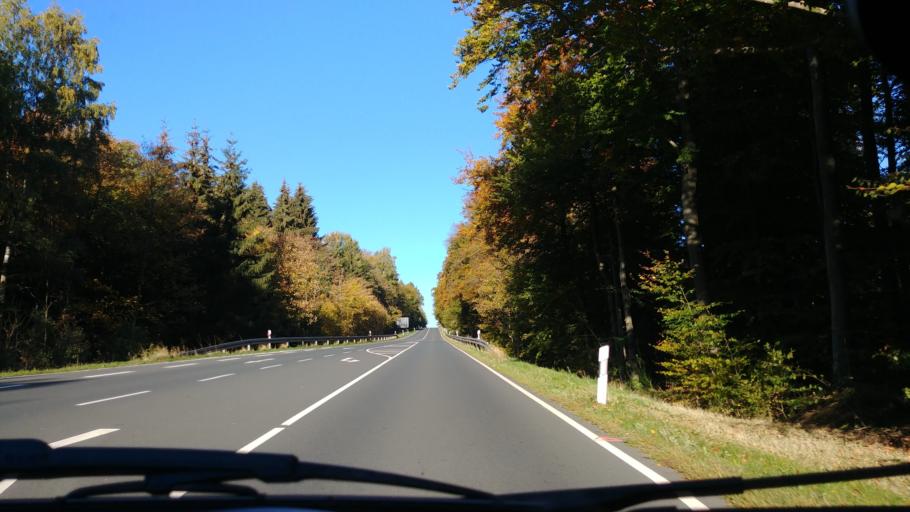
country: DE
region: Rheinland-Pfalz
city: Reckenroth
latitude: 50.1804
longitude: 7.9834
